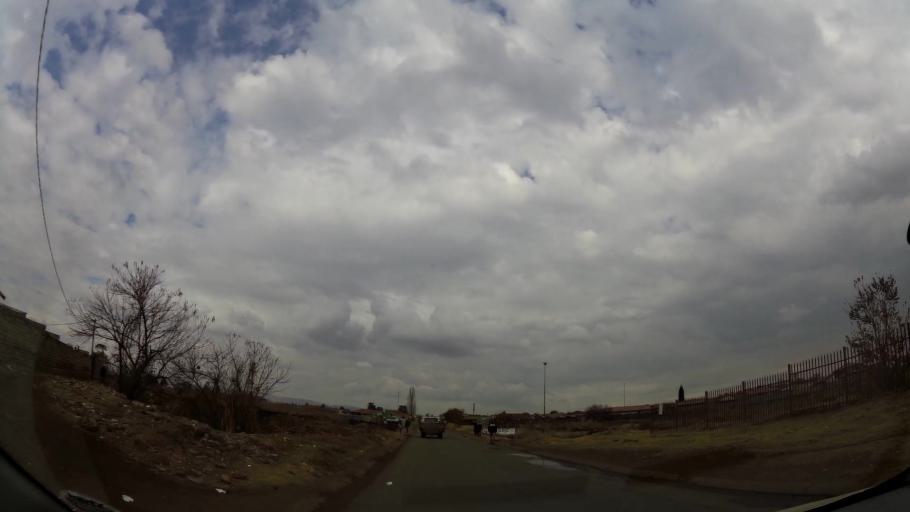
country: ZA
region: Gauteng
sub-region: Ekurhuleni Metropolitan Municipality
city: Germiston
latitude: -26.3830
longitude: 28.1575
